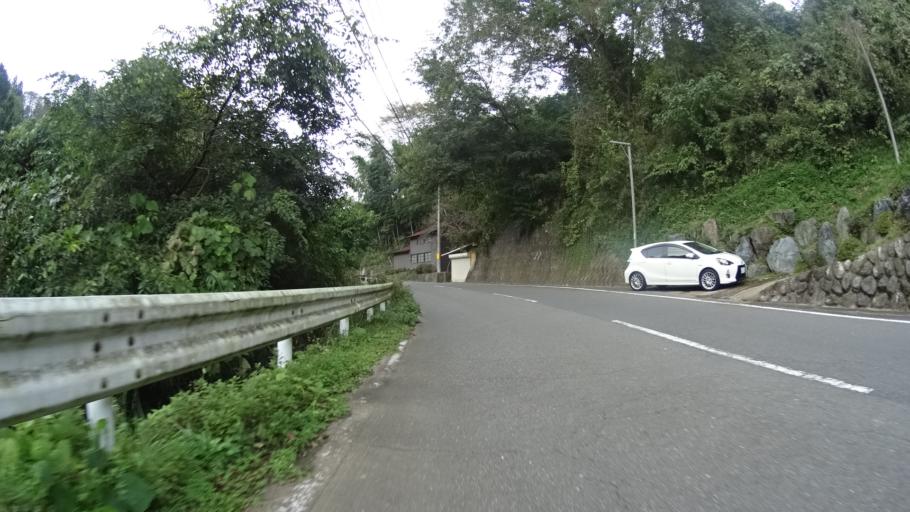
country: JP
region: Yamanashi
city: Uenohara
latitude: 35.6374
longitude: 139.0671
